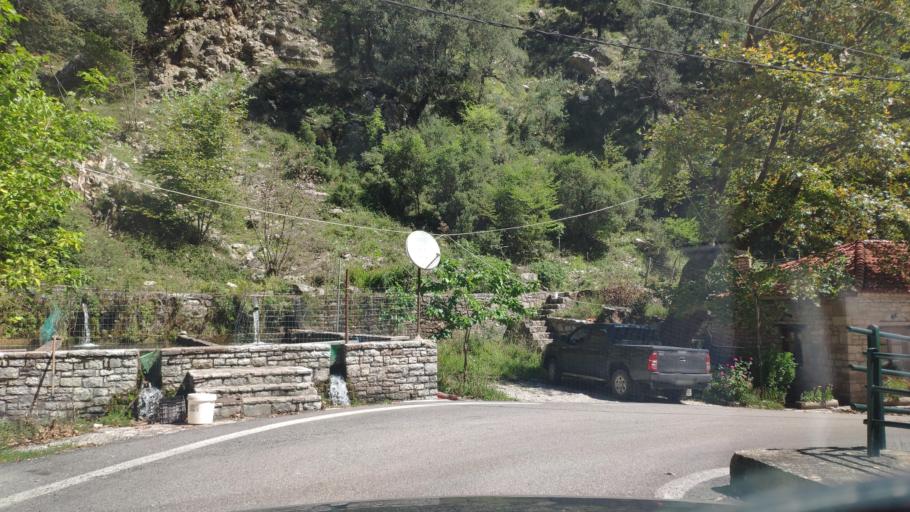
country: GR
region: Central Greece
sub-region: Nomos Evrytanias
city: Kerasochori
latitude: 39.1370
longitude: 21.6378
